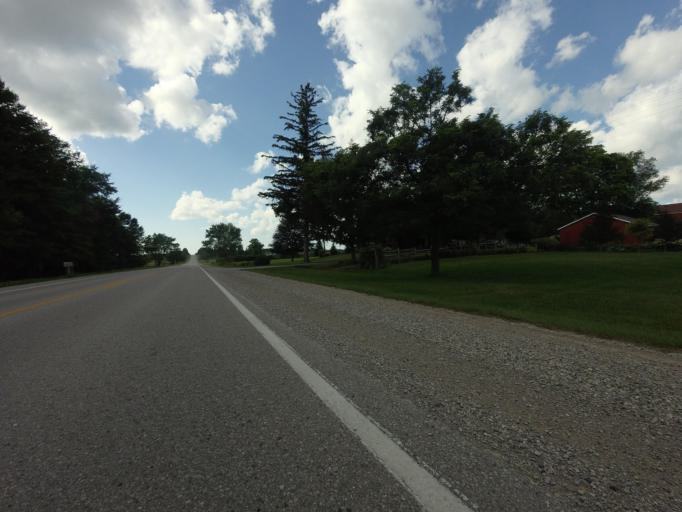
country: CA
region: Ontario
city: Huron East
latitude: 43.7383
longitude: -81.4511
